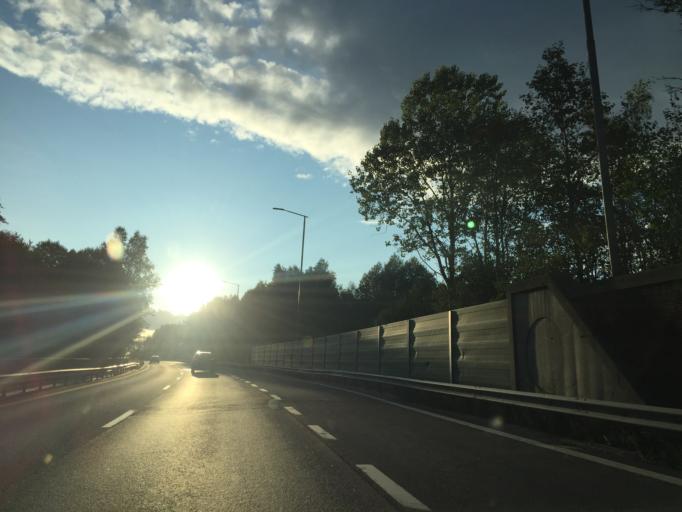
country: NO
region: Akershus
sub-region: Lorenskog
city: Kjenn
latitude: 59.9400
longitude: 10.9261
